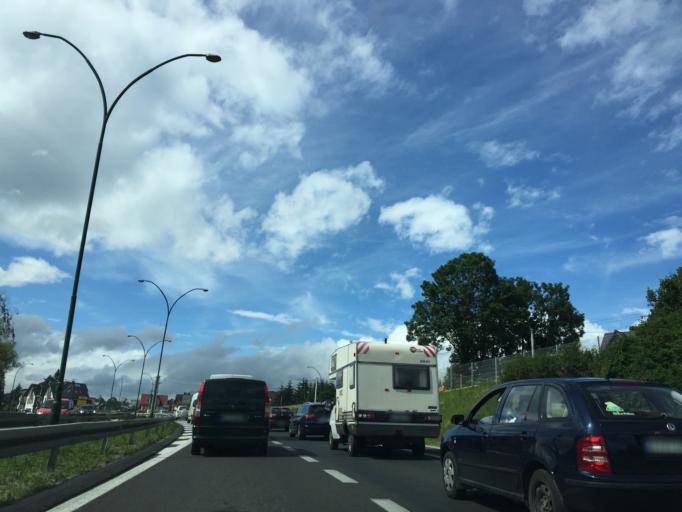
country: PL
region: Lesser Poland Voivodeship
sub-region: Powiat nowotarski
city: Nowy Targ
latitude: 49.4890
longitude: 20.0181
